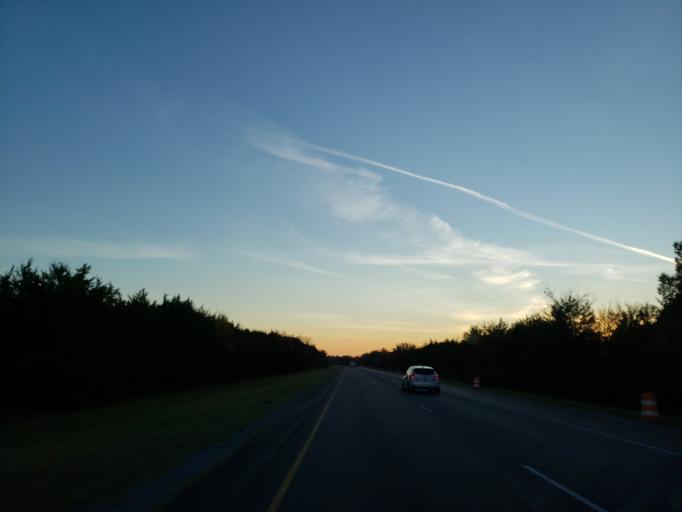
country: US
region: Alabama
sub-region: Sumter County
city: Livingston
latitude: 32.6514
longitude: -88.1913
